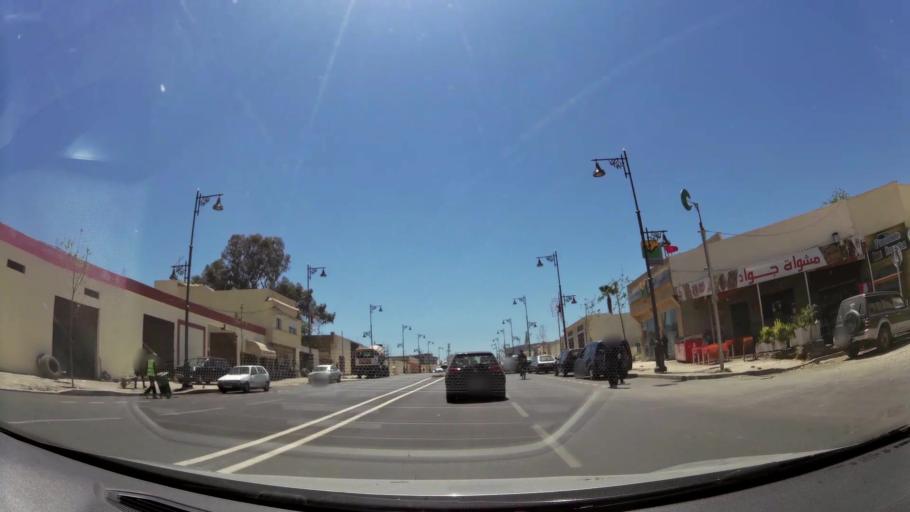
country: MA
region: Meknes-Tafilalet
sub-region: Meknes
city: Meknes
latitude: 33.8666
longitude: -5.5367
